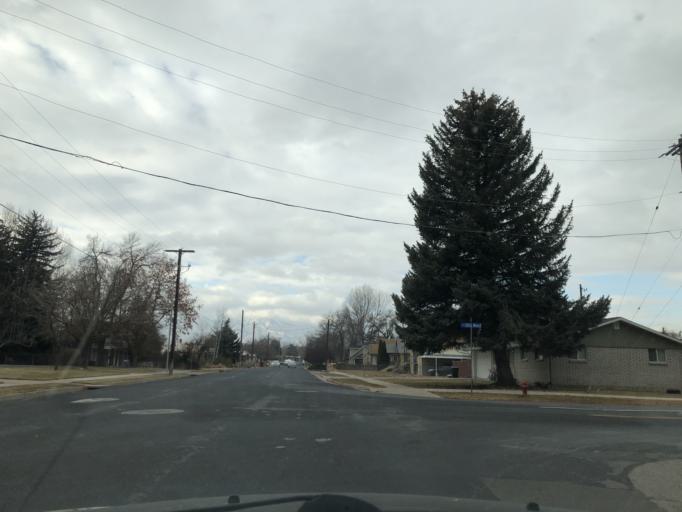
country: US
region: Utah
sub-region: Cache County
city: Logan
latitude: 41.7208
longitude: -111.8377
